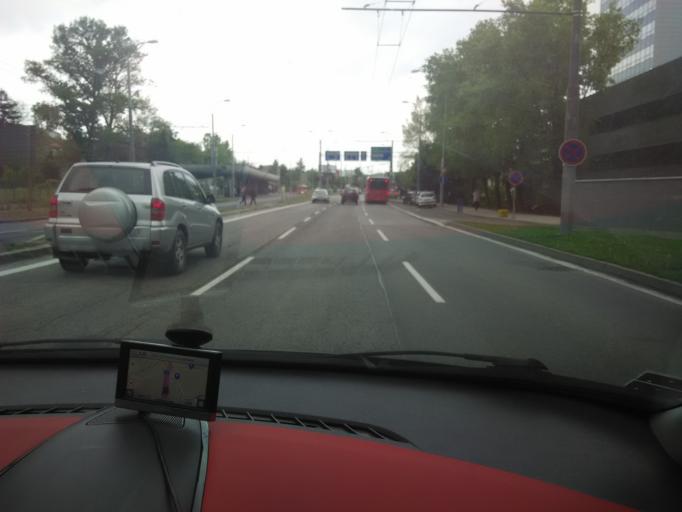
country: SK
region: Bratislavsky
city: Bratislava
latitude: 48.1697
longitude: 17.0746
